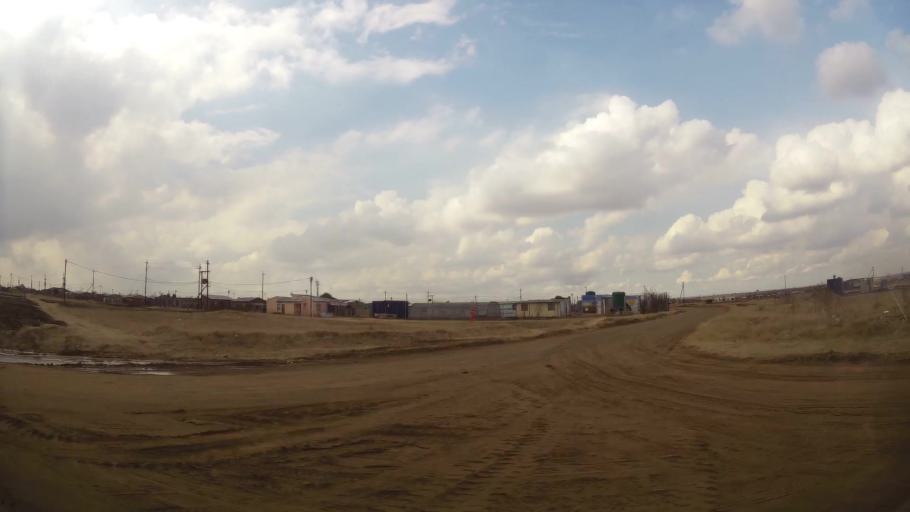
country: ZA
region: Orange Free State
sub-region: Fezile Dabi District Municipality
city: Sasolburg
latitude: -26.8623
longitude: 27.8952
